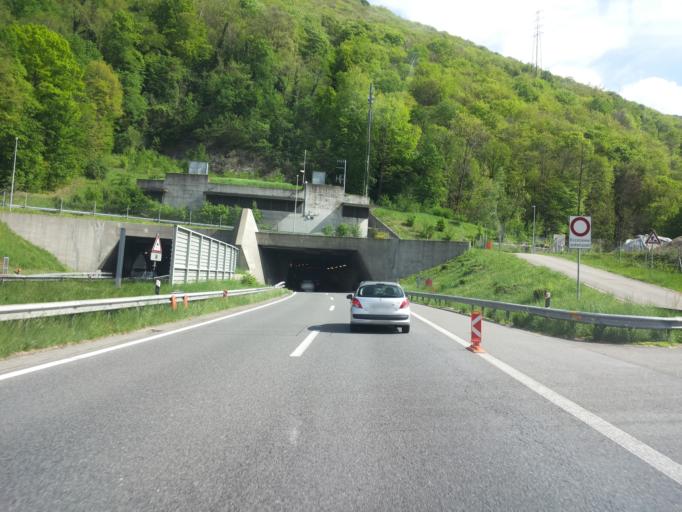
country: CH
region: Ticino
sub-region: Lugano District
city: Montagnola
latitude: 45.9645
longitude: 8.9263
